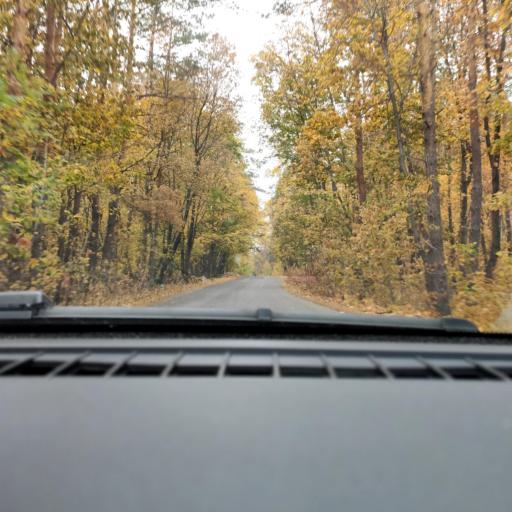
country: RU
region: Voronezj
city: Somovo
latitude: 51.6870
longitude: 39.2999
